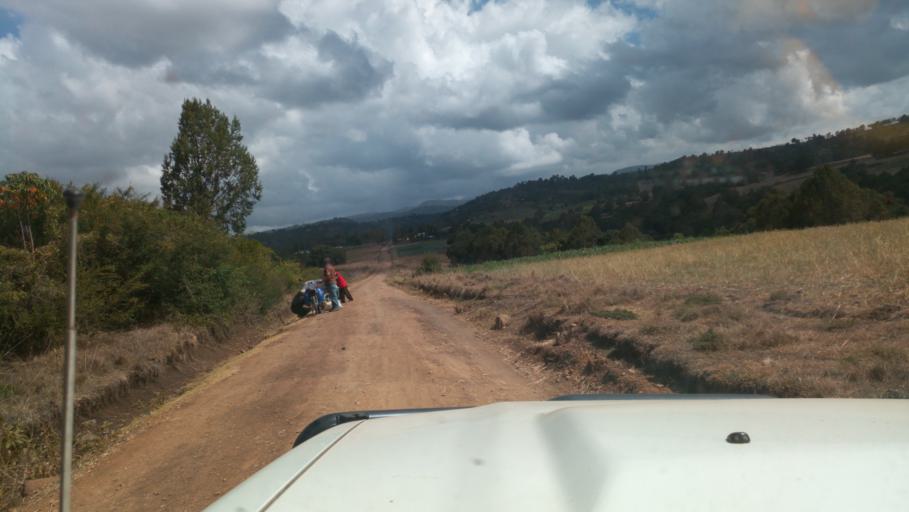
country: KE
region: Laikipia
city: Naro Moru
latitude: -0.1878
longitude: 36.7070
